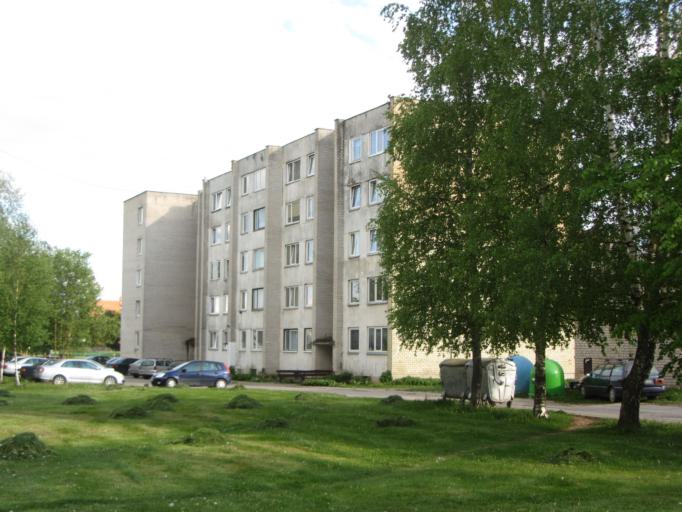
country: LT
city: Sirvintos
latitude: 55.0446
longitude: 24.9494
